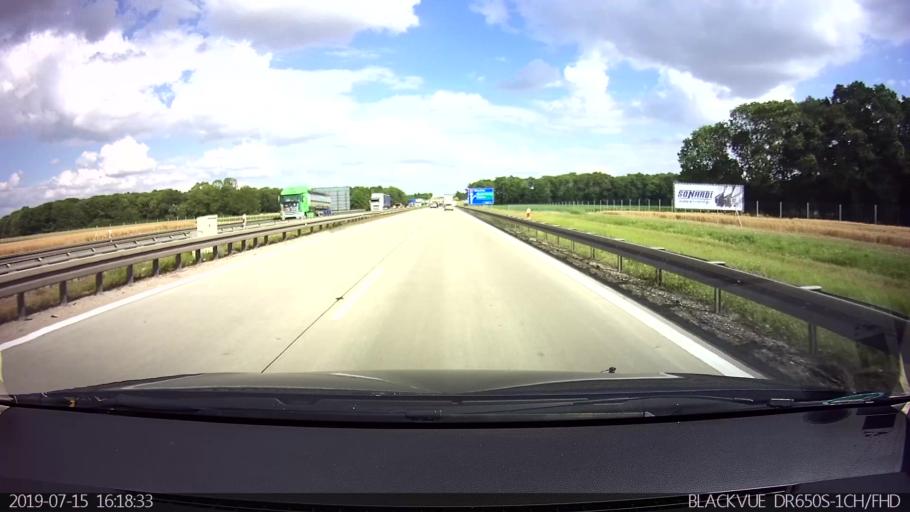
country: PL
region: Lower Silesian Voivodeship
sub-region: Powiat sredzki
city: Udanin
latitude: 51.0774
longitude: 16.4423
